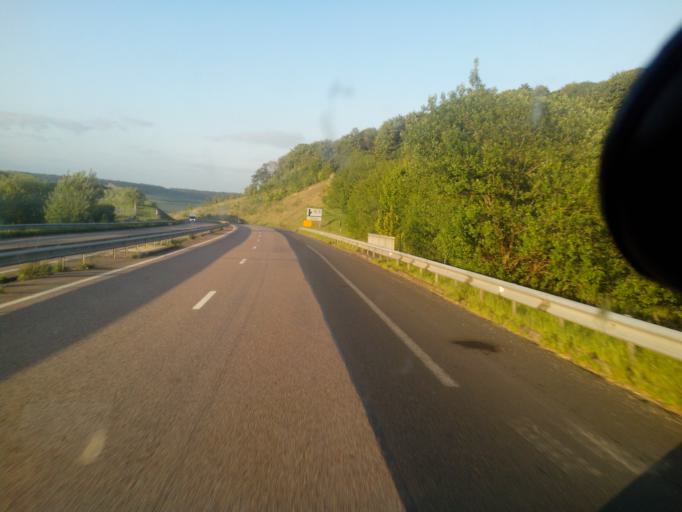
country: FR
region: Haute-Normandie
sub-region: Departement de la Seine-Maritime
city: Blangy-sur-Bresle
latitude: 49.9112
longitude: 1.6242
